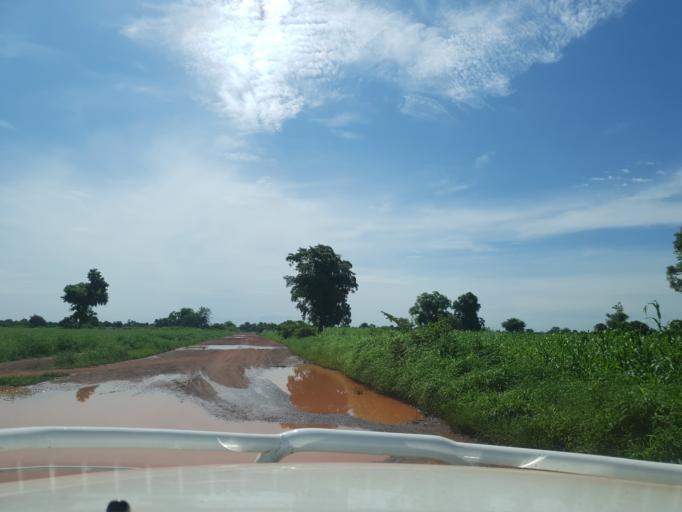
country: ML
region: Koulikoro
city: Banamba
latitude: 13.2758
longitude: -7.5457
